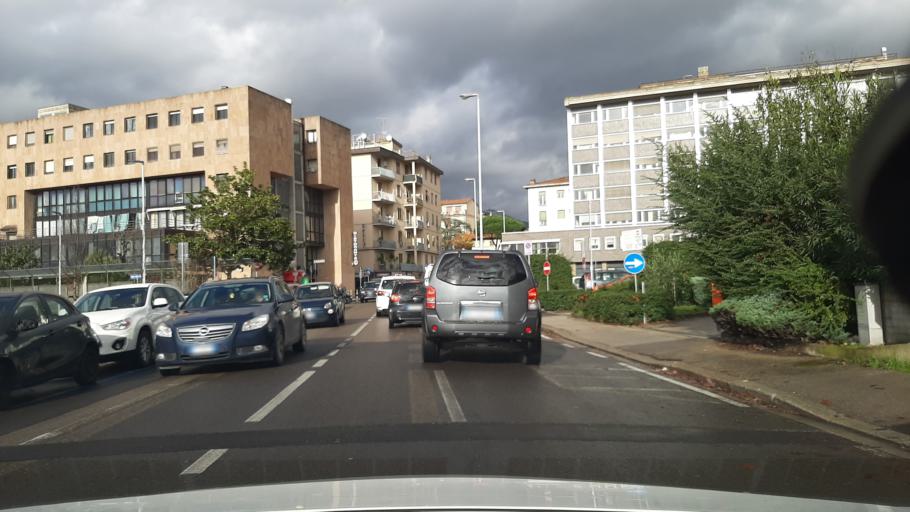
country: IT
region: Tuscany
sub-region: Province of Florence
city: Florence
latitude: 43.7962
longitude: 11.2448
